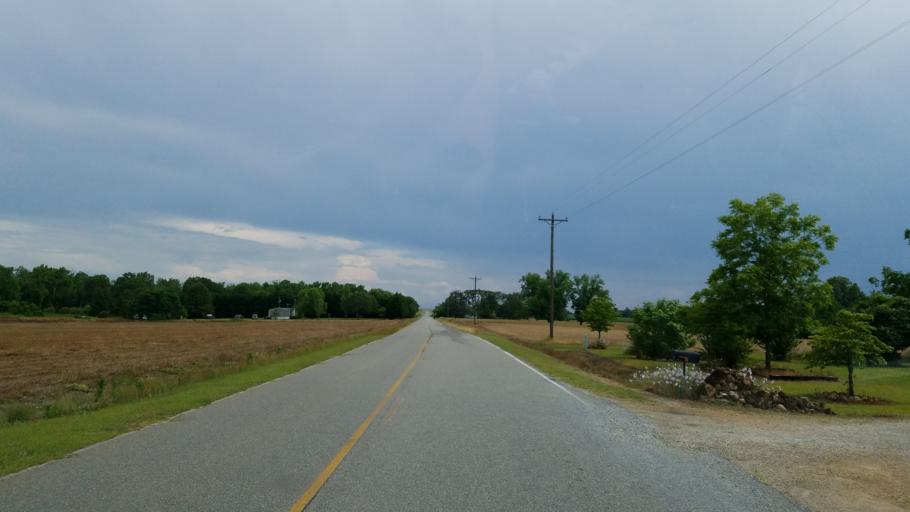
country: US
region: Georgia
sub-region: Dooly County
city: Unadilla
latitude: 32.3025
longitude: -83.7918
